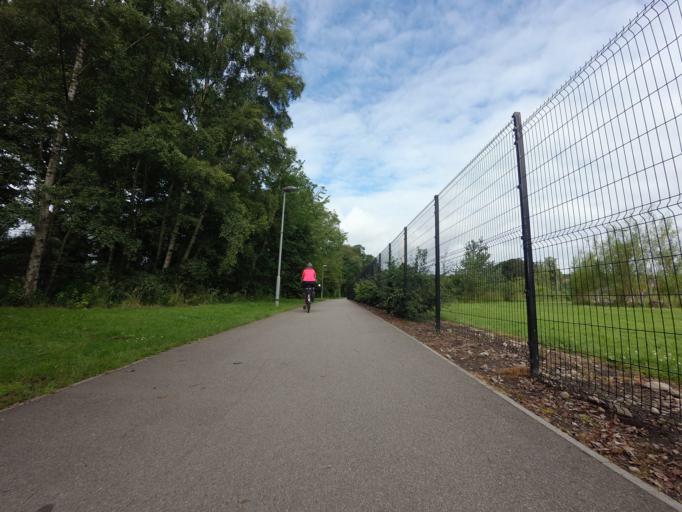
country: GB
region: Scotland
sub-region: Moray
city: Elgin
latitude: 57.6510
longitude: -3.3286
